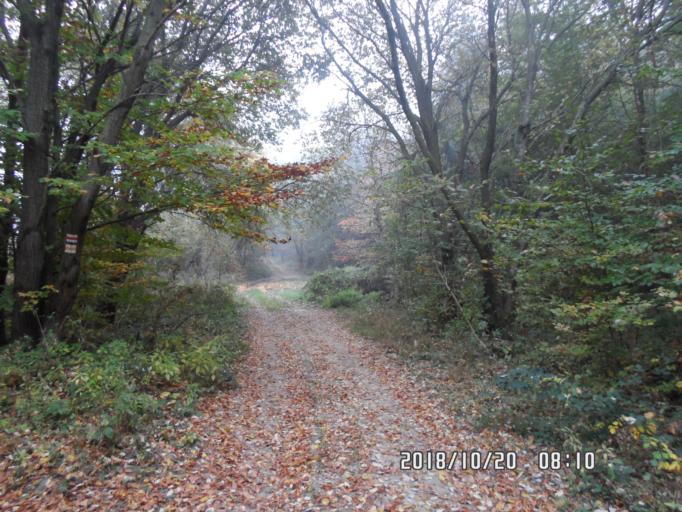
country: HU
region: Veszprem
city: Herend
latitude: 47.2049
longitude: 17.7599
